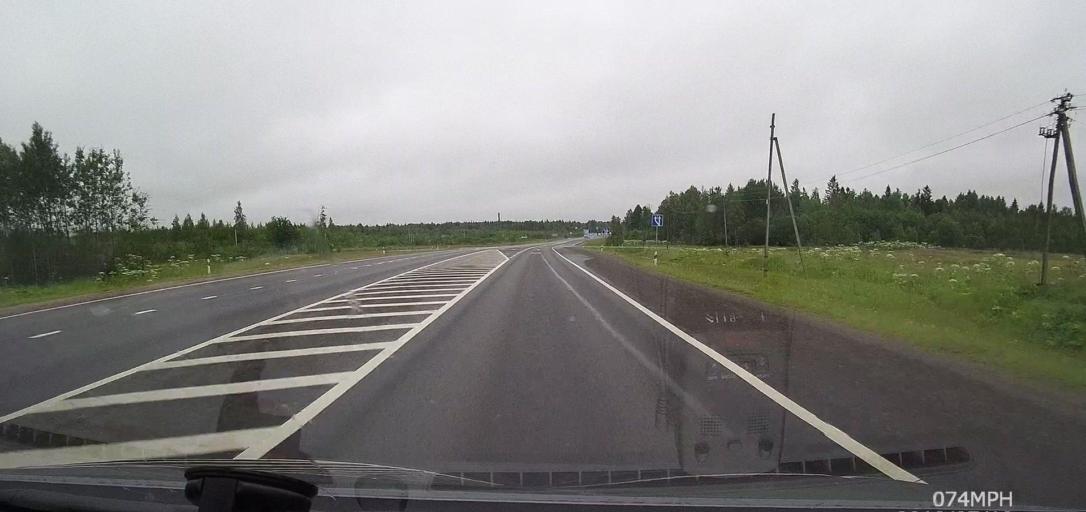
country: RU
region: Leningrad
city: Staraya Ladoga
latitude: 59.9959
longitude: 32.0982
